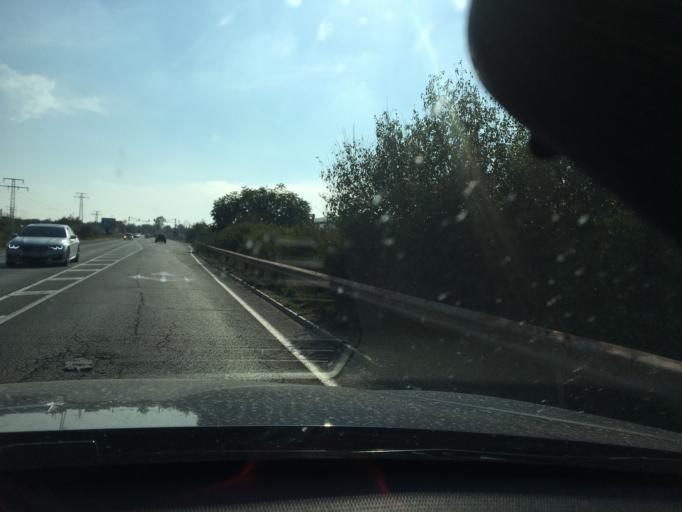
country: BG
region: Burgas
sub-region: Obshtina Nesebur
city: Ravda
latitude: 42.6655
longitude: 27.6937
